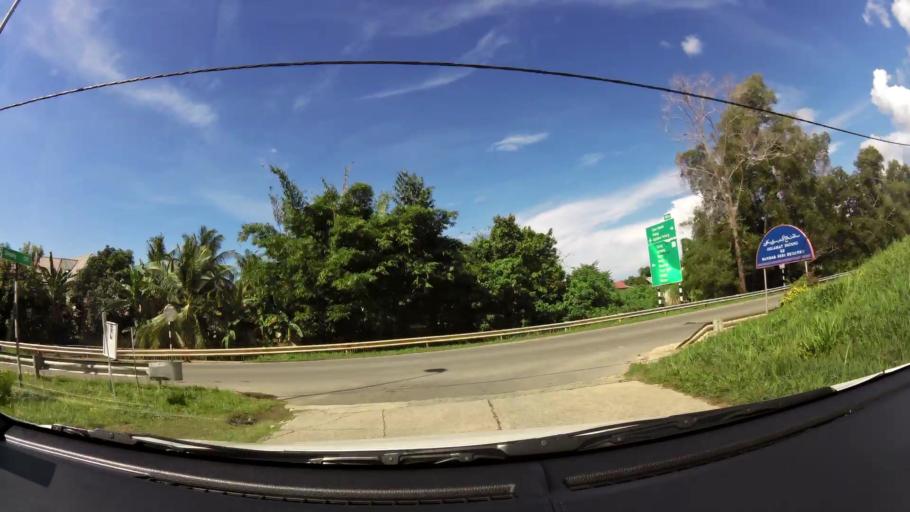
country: BN
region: Brunei and Muara
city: Bandar Seri Begawan
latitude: 4.9542
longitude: 114.9450
